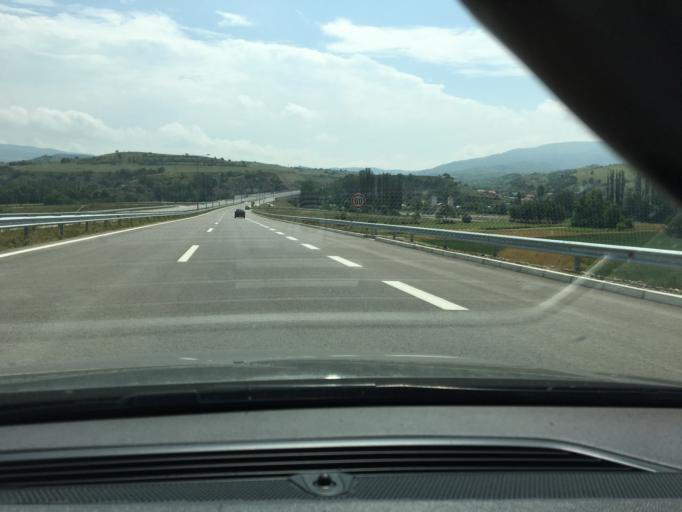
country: MK
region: Petrovec
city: Sredno Konjare
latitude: 41.9625
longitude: 21.7100
